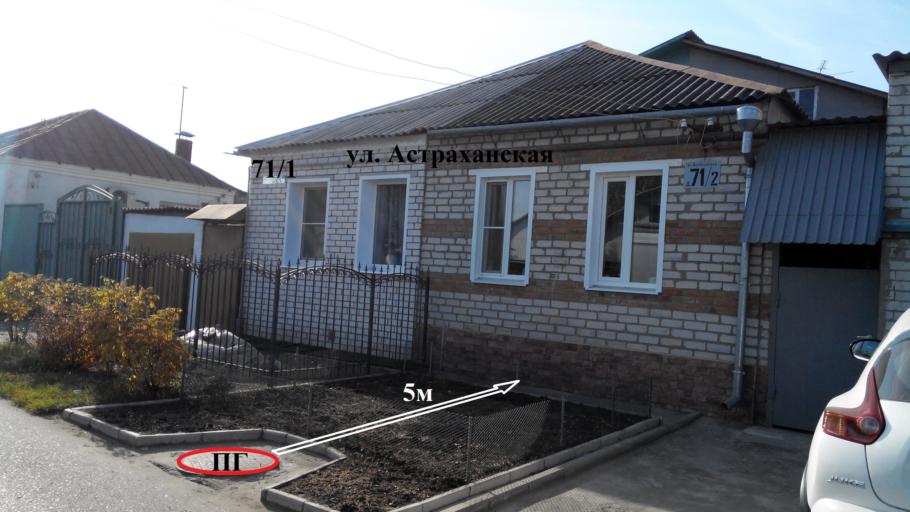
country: RU
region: Voronezj
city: Voronezh
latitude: 51.6315
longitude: 39.1652
